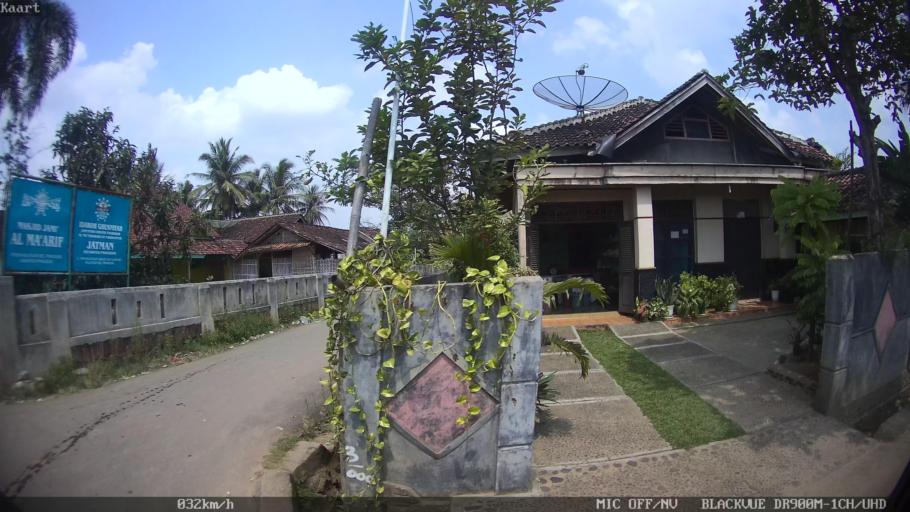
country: ID
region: Lampung
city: Pringsewu
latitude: -5.3780
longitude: 104.9663
